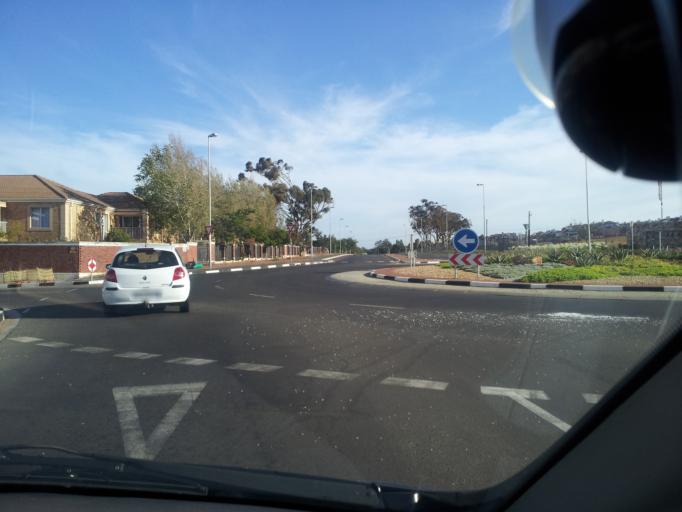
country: ZA
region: Western Cape
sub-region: City of Cape Town
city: Kraaifontein
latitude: -33.8184
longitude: 18.6348
